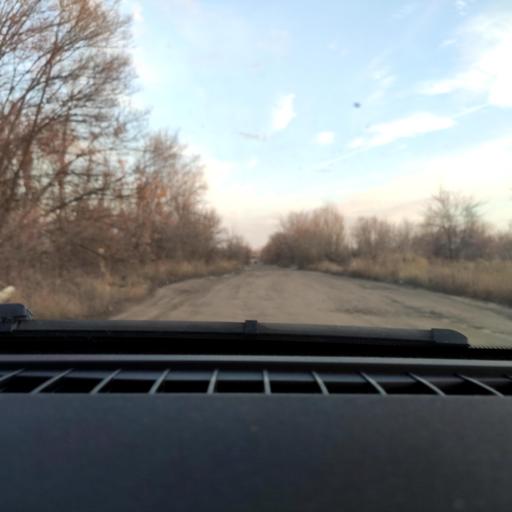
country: RU
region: Voronezj
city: Maslovka
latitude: 51.6082
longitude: 39.2663
